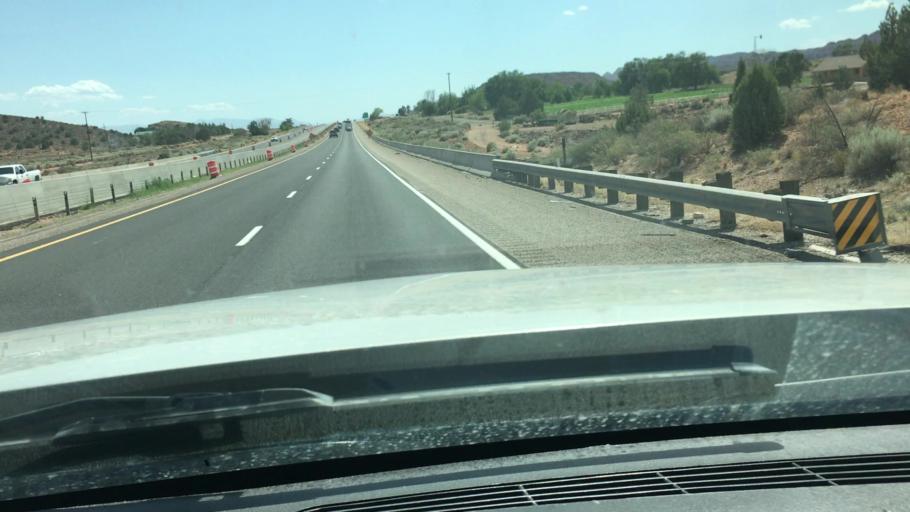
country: US
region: Utah
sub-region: Washington County
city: Toquerville
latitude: 37.2510
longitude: -113.3428
